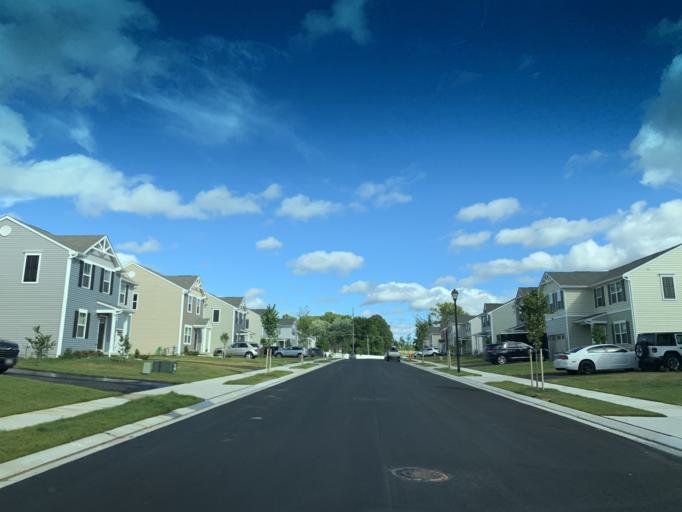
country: US
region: Maryland
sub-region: Baltimore County
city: Middle River
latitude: 39.3561
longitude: -76.4358
